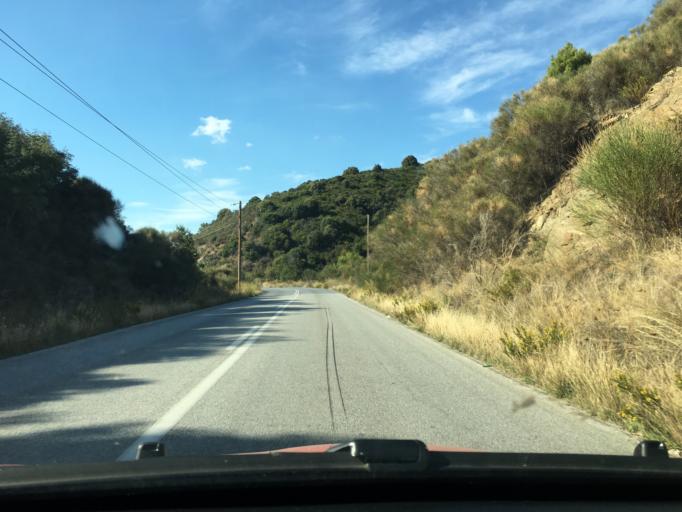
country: GR
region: Central Macedonia
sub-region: Nomos Chalkidikis
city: Ierissos
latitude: 40.3862
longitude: 23.8187
